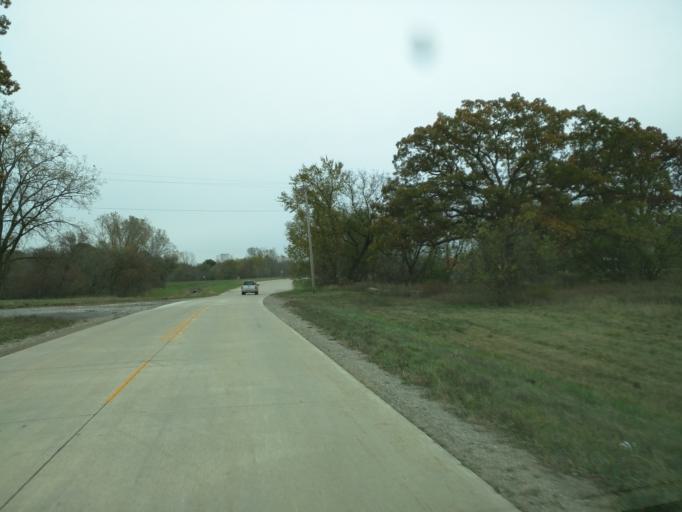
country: US
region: Michigan
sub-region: Ingham County
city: Edgemont Park
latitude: 42.7732
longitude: -84.5689
